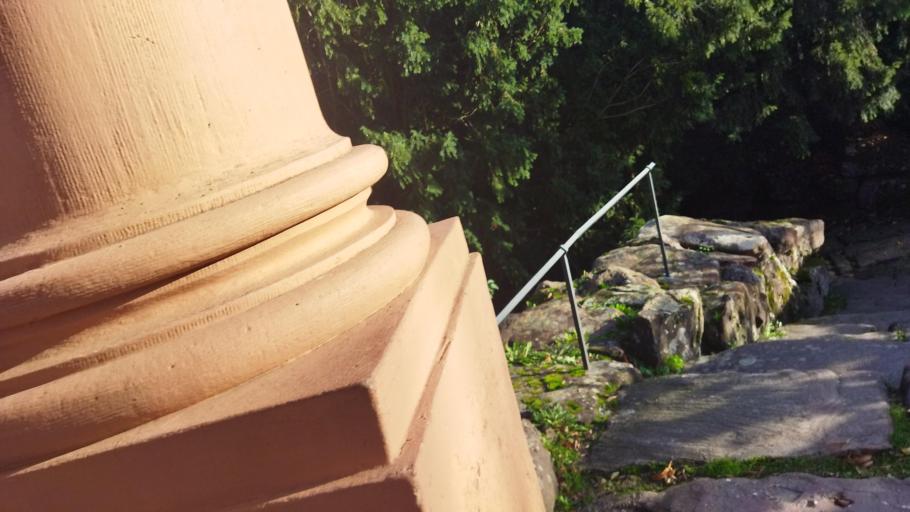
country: DE
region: Baden-Wuerttemberg
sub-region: Karlsruhe Region
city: Schwetzingen
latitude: 49.3851
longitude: 8.5632
